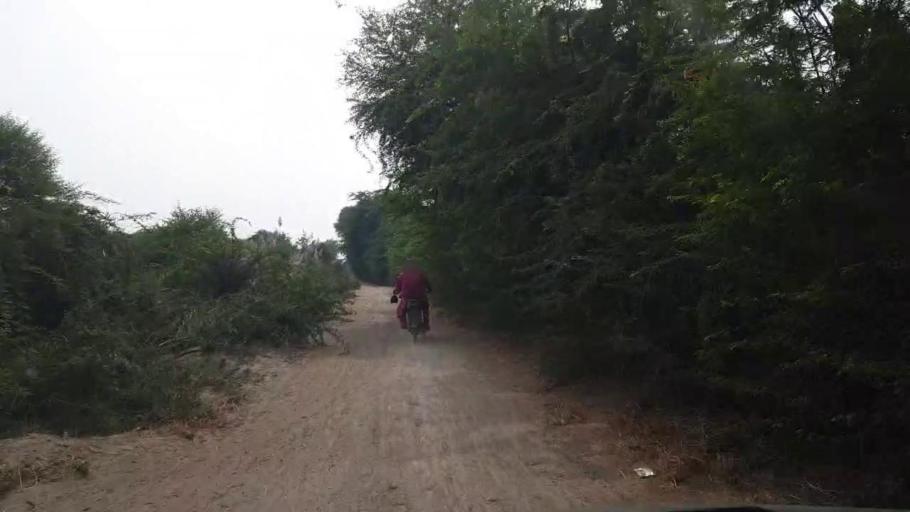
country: PK
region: Sindh
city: Matli
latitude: 24.9930
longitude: 68.7028
